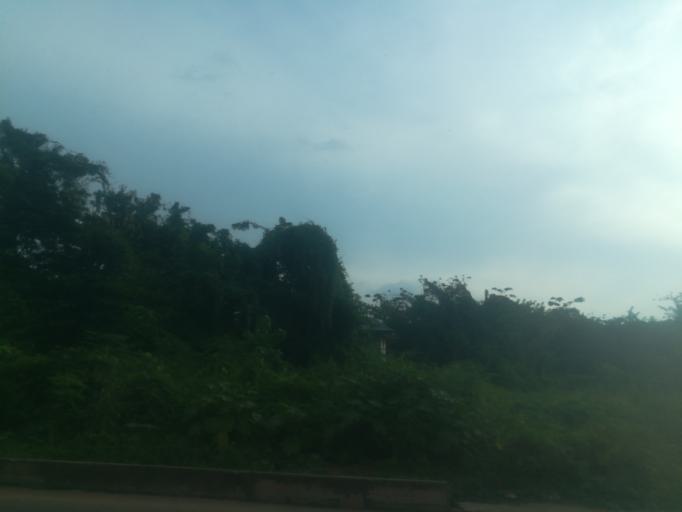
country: NG
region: Ogun
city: Abeokuta
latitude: 7.1621
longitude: 3.3175
